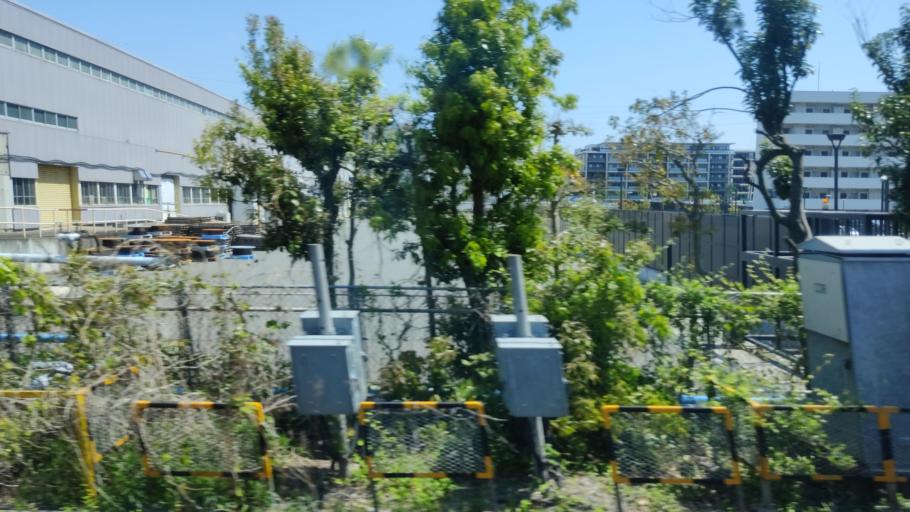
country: JP
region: Kanagawa
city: Fujisawa
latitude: 35.4106
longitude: 139.5353
